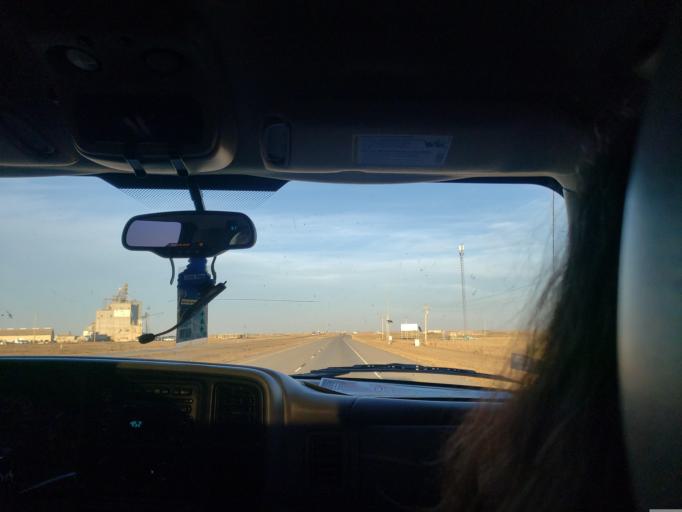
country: US
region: Oklahoma
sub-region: Texas County
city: Guymon
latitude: 36.7674
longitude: -101.3454
